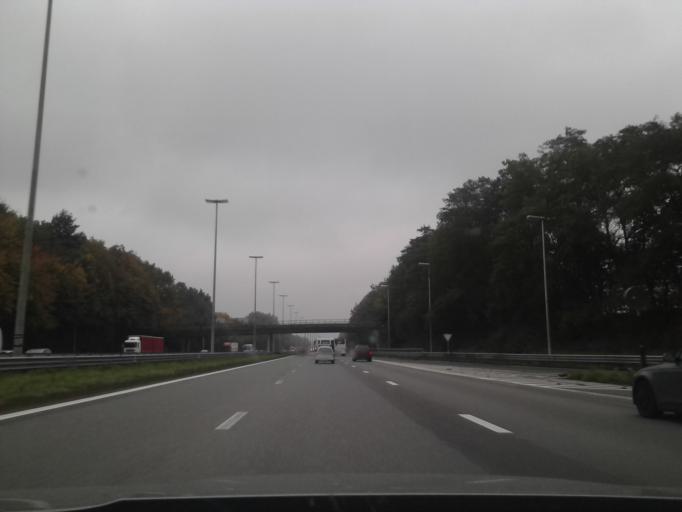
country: BE
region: Wallonia
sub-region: Province du Brabant Wallon
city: Braine-le-Chateau
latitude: 50.6559
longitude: 4.3099
